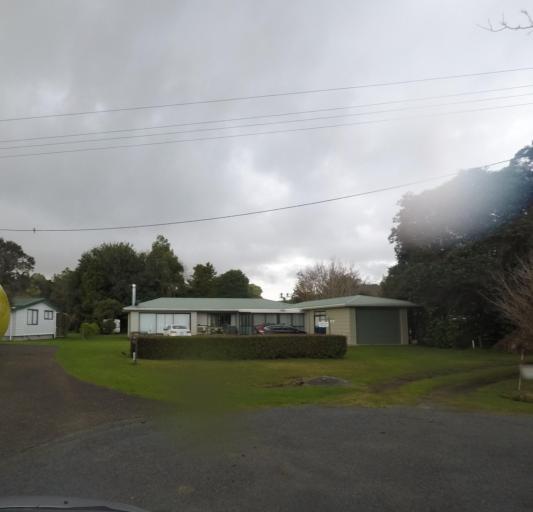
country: NZ
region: Auckland
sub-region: Auckland
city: Warkworth
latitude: -36.3830
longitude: 174.7662
